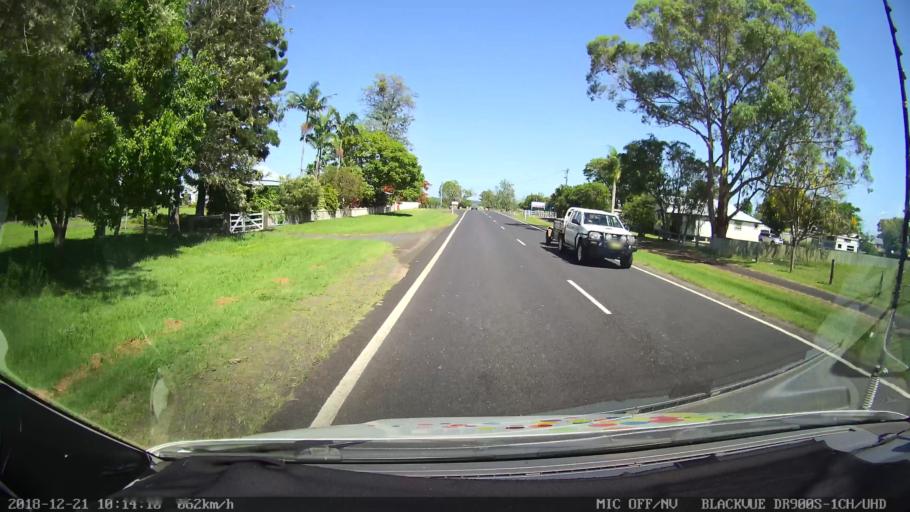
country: AU
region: New South Wales
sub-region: Clarence Valley
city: South Grafton
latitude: -29.6961
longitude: 152.9155
